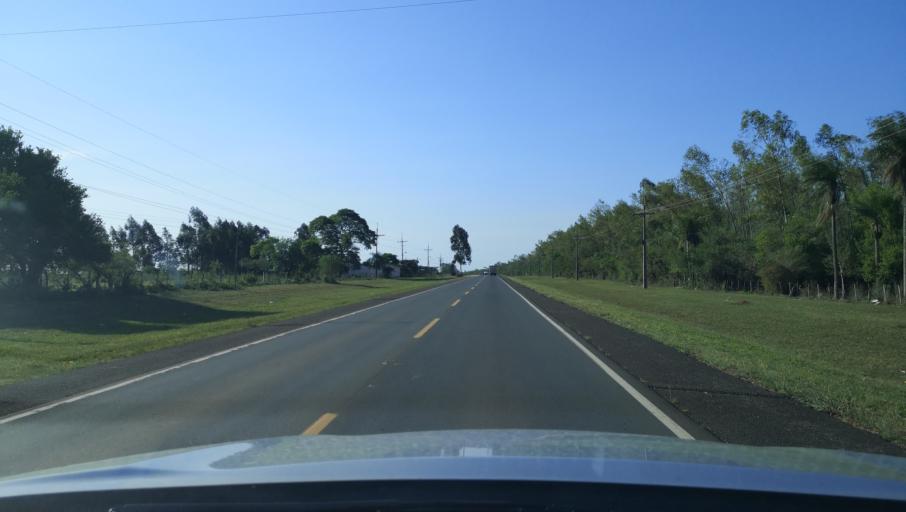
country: PY
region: Misiones
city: Santa Maria
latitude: -26.7660
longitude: -57.0322
